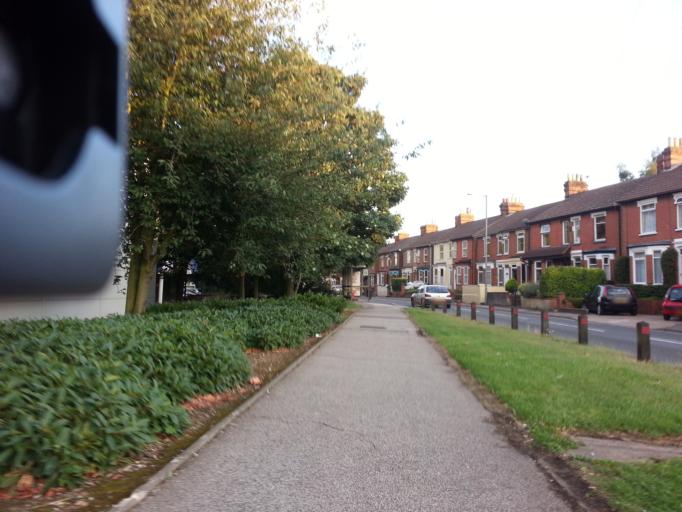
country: GB
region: England
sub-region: Suffolk
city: Ipswich
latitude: 52.0558
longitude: 1.1331
